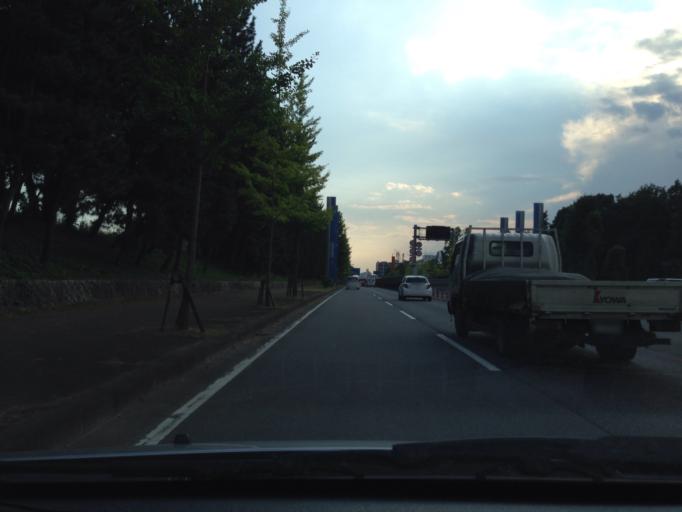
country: JP
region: Ibaraki
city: Naka
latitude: 36.0854
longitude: 140.1249
